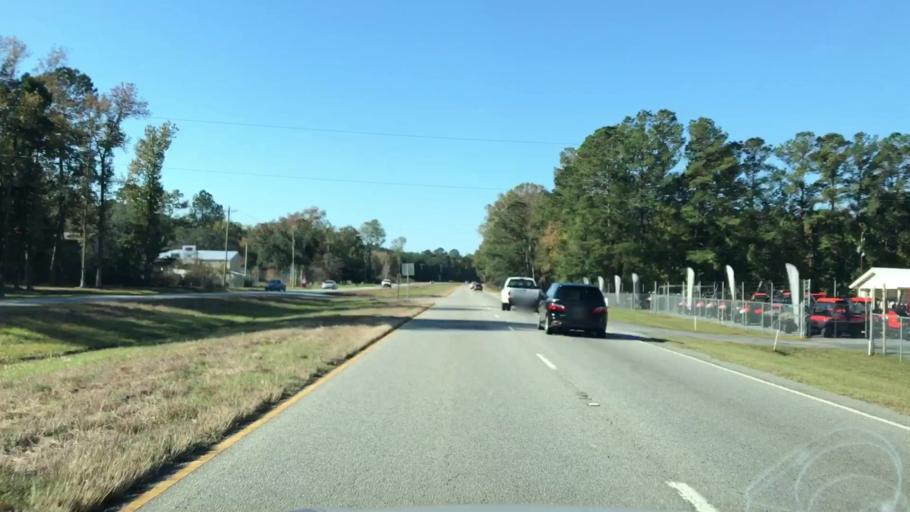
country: US
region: South Carolina
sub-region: Charleston County
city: Ravenel
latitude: 32.7574
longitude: -80.3223
